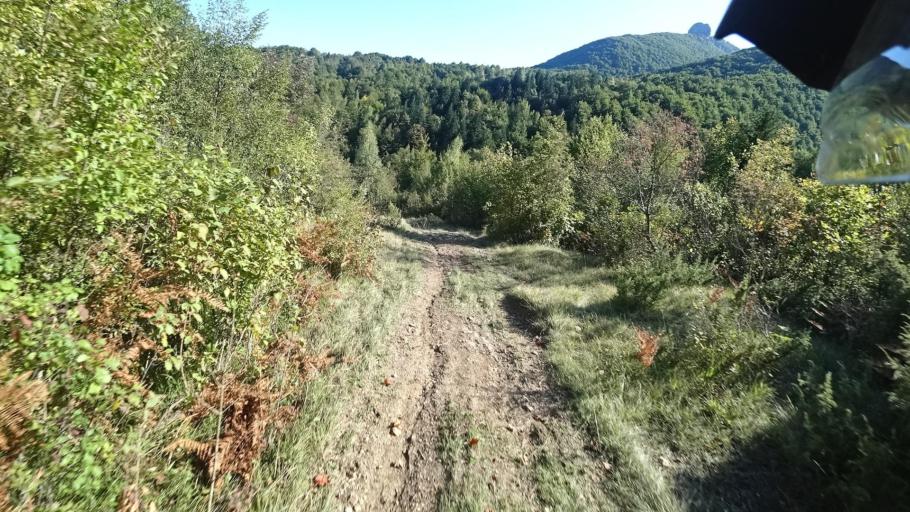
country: HR
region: Karlovacka
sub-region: Grad Ogulin
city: Ogulin
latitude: 45.2836
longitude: 15.1409
